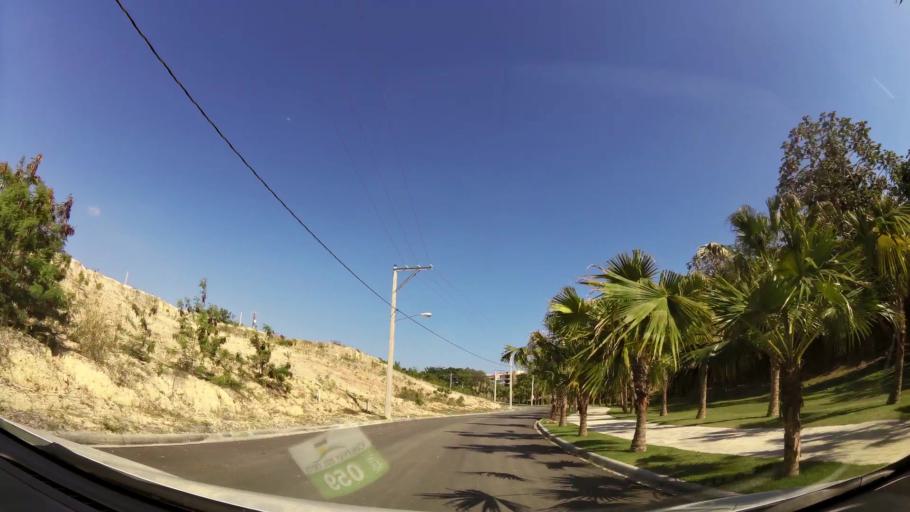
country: DO
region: Nacional
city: Santo Domingo
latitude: 18.4608
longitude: -69.9858
